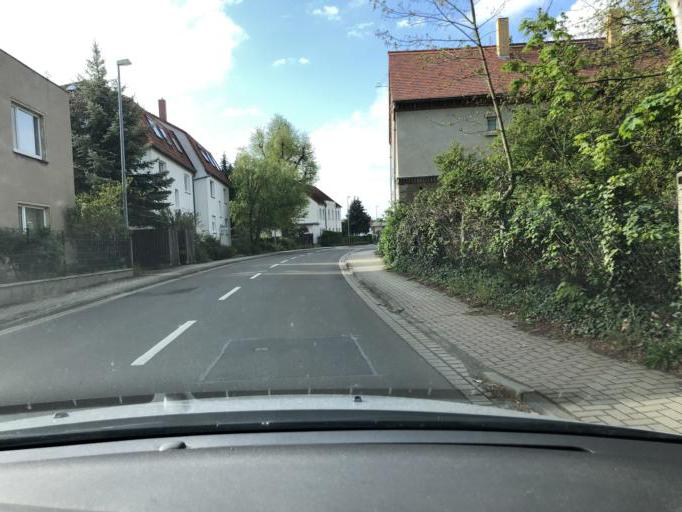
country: DE
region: Saxony
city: Bohlen
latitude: 51.2386
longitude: 12.3850
